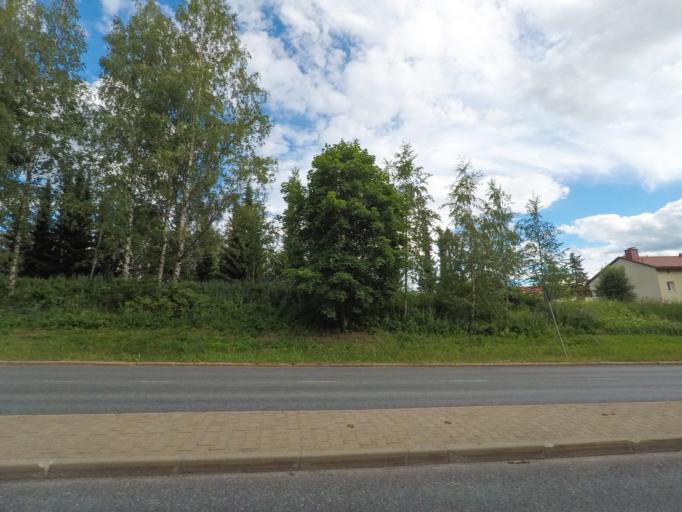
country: FI
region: Paijanne Tavastia
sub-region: Lahti
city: Lahti
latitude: 60.9732
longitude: 25.6346
